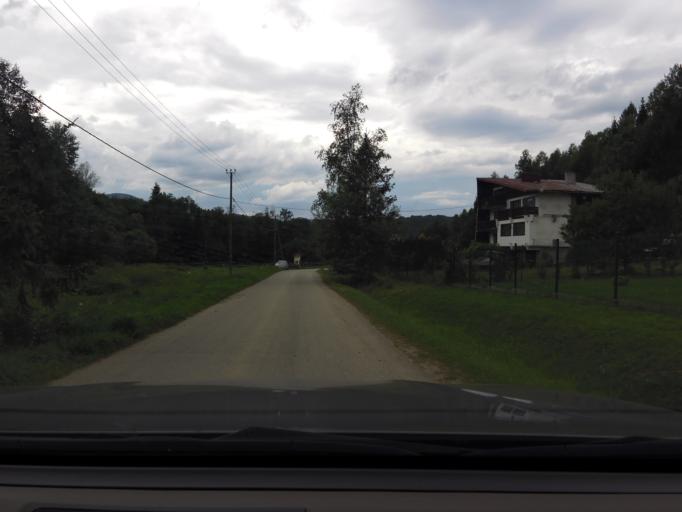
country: PL
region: Silesian Voivodeship
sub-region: Powiat zywiecki
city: Ujsoly
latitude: 49.5051
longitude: 19.1394
